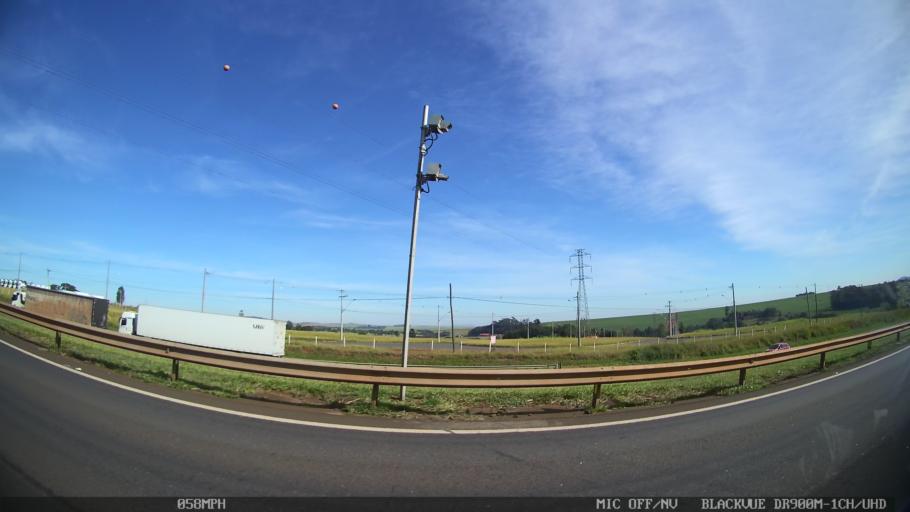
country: BR
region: Sao Paulo
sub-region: Araras
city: Araras
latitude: -22.4010
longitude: -47.3895
